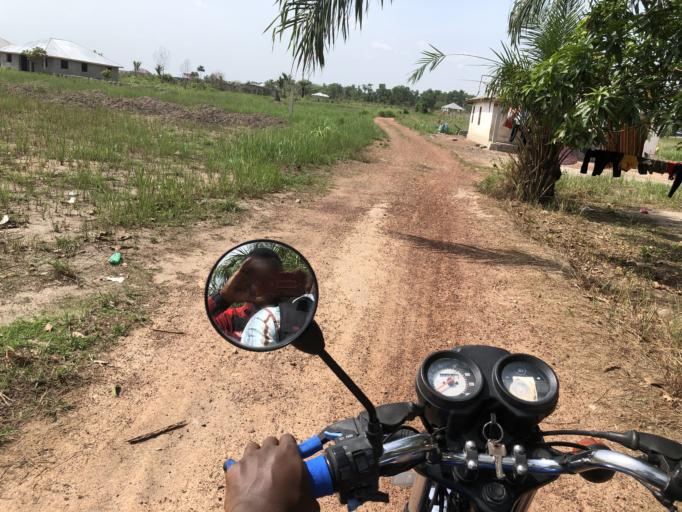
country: SL
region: Northern Province
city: Yonibana
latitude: 8.4702
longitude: -12.2336
